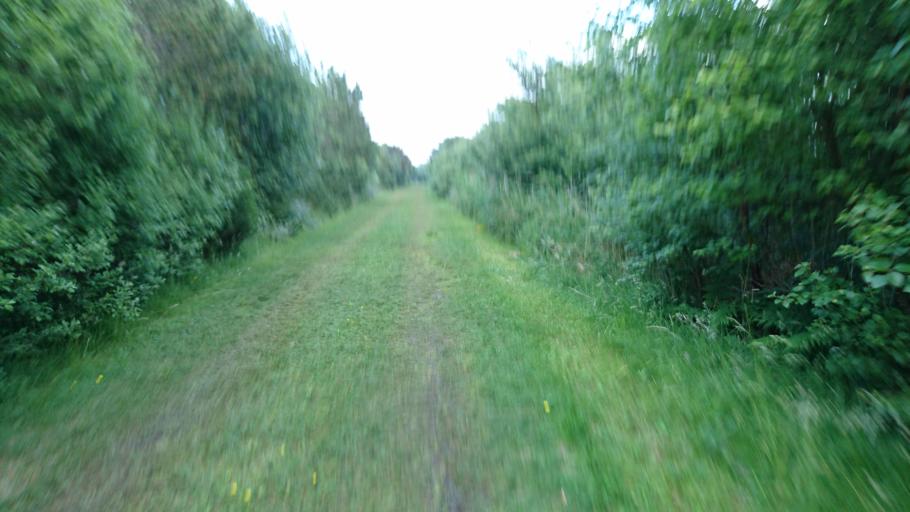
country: DK
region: North Denmark
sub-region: Frederikshavn Kommune
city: Skagen
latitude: 57.7417
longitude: 10.6045
